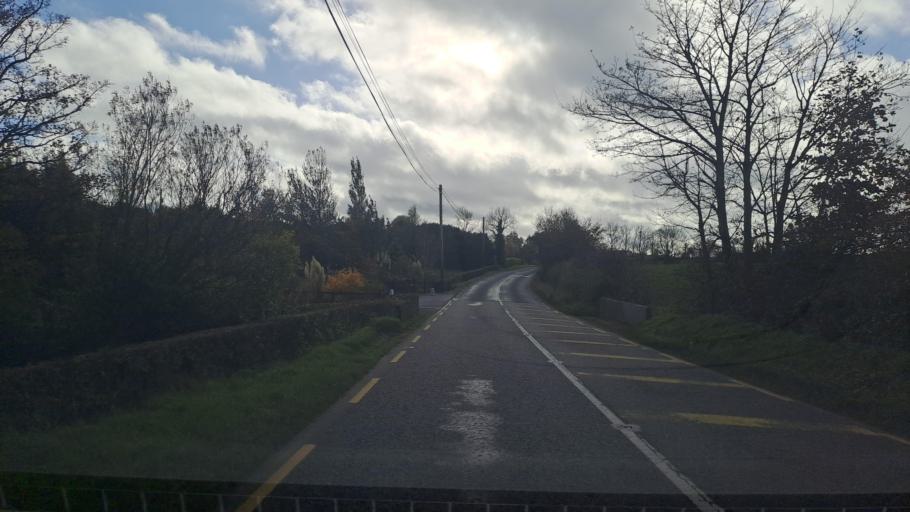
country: IE
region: Ulster
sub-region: County Monaghan
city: Monaghan
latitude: 54.2063
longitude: -6.9865
